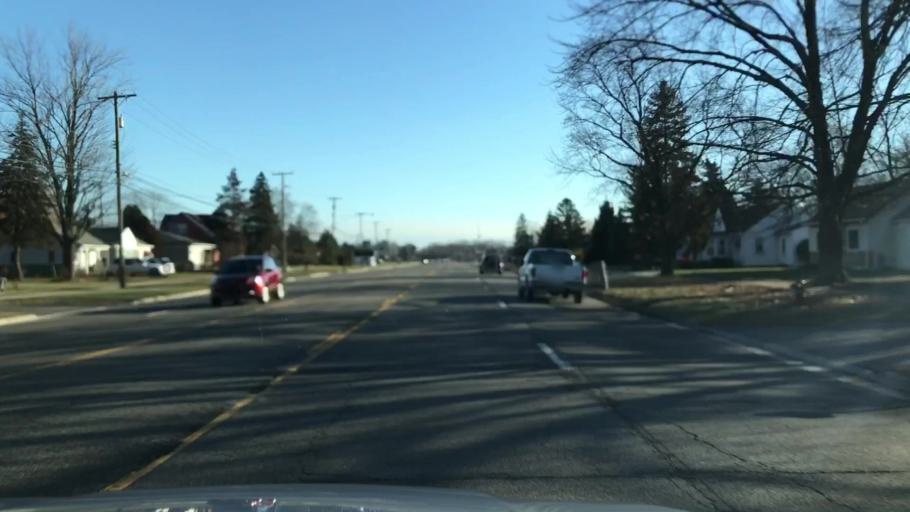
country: US
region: Michigan
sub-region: Oakland County
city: Clawson
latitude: 42.5493
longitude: -83.0954
